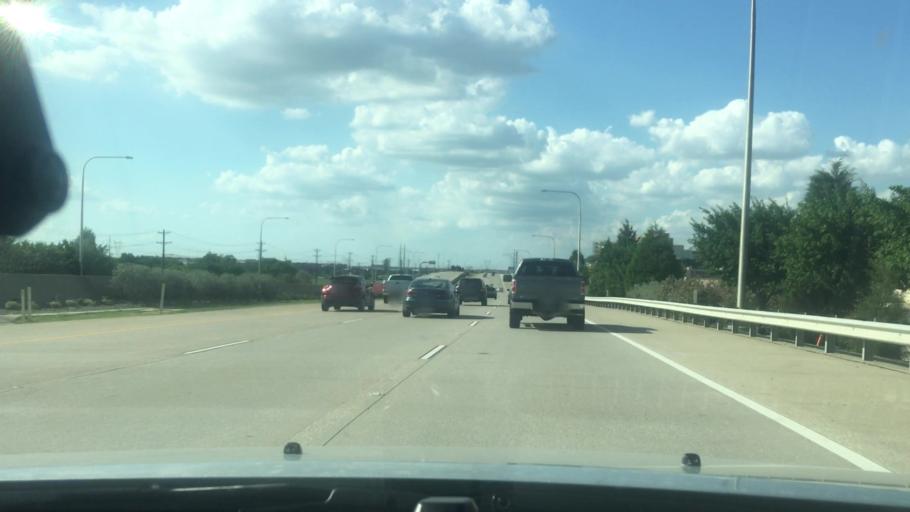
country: US
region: Texas
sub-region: Collin County
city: Frisco
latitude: 33.1464
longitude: -96.8393
